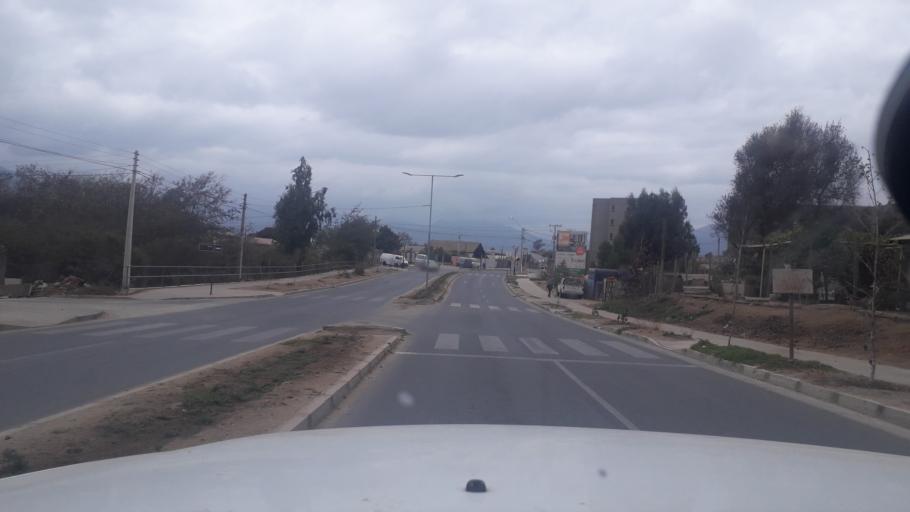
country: CL
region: Valparaiso
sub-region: Provincia de Marga Marga
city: Limache
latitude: -33.0148
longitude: -71.2674
